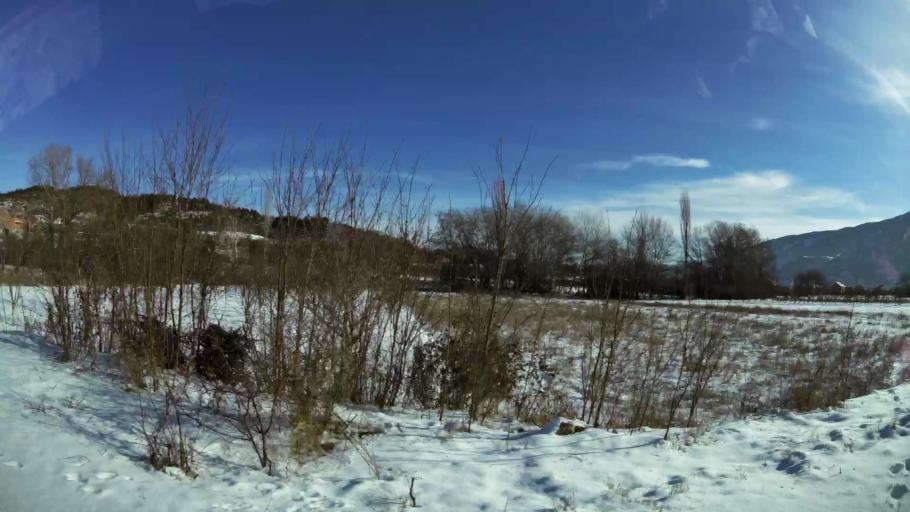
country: MK
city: Ljubin
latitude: 41.9839
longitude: 21.2988
